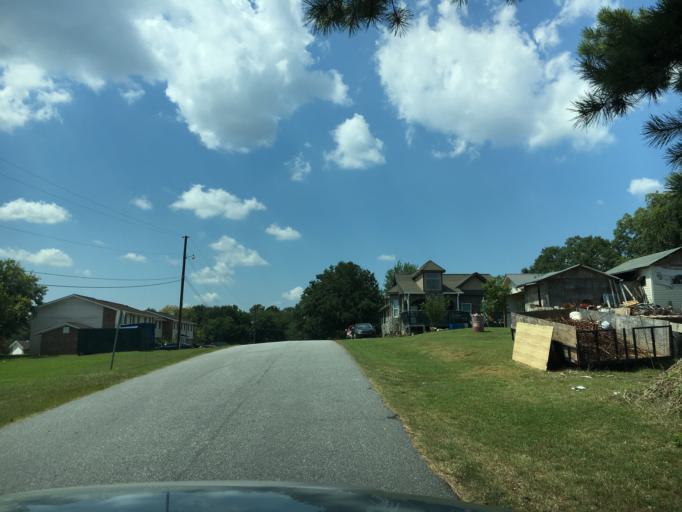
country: US
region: South Carolina
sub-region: Spartanburg County
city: Duncan
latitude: 34.9306
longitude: -82.1303
